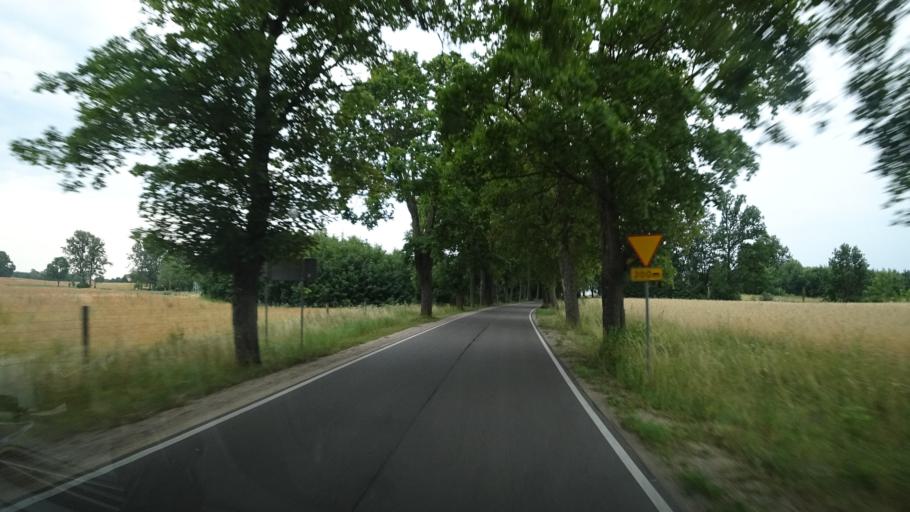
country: PL
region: Warmian-Masurian Voivodeship
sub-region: Powiat mragowski
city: Mikolajki
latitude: 53.8541
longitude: 21.6141
